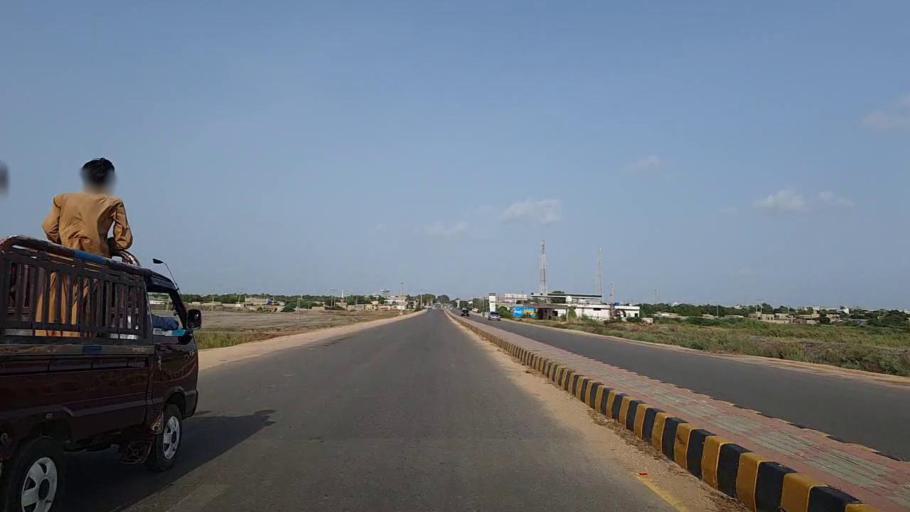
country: PK
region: Sindh
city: Thatta
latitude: 24.7443
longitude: 67.8778
